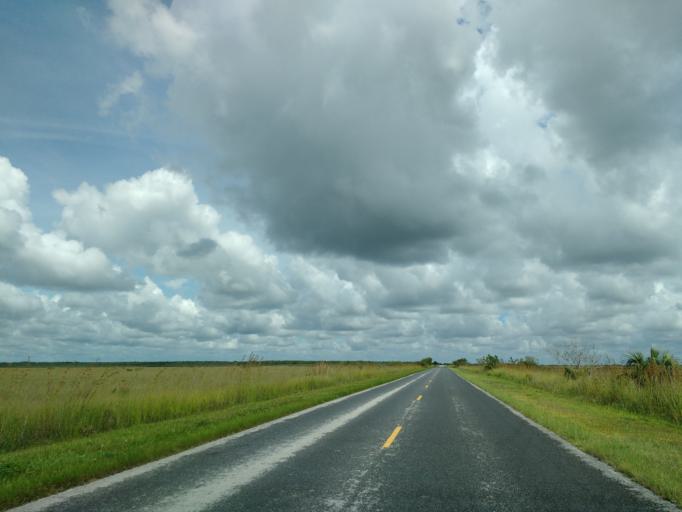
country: US
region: Florida
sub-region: Miami-Dade County
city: Florida City
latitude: 25.3970
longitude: -80.5966
